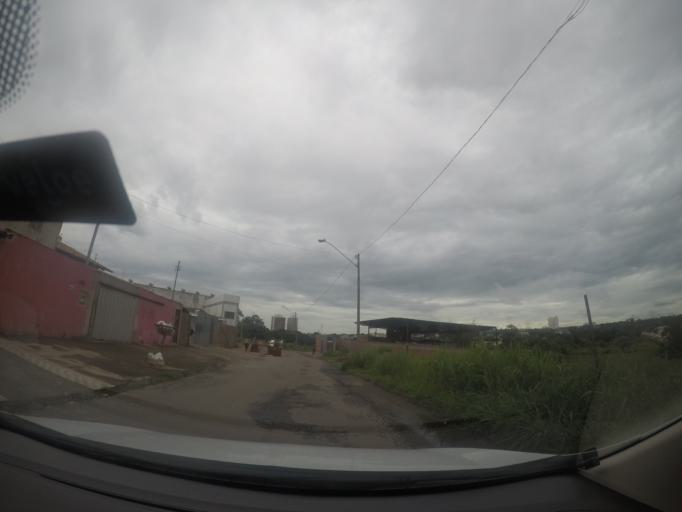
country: BR
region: Goias
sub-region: Goiania
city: Goiania
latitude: -16.6632
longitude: -49.3122
